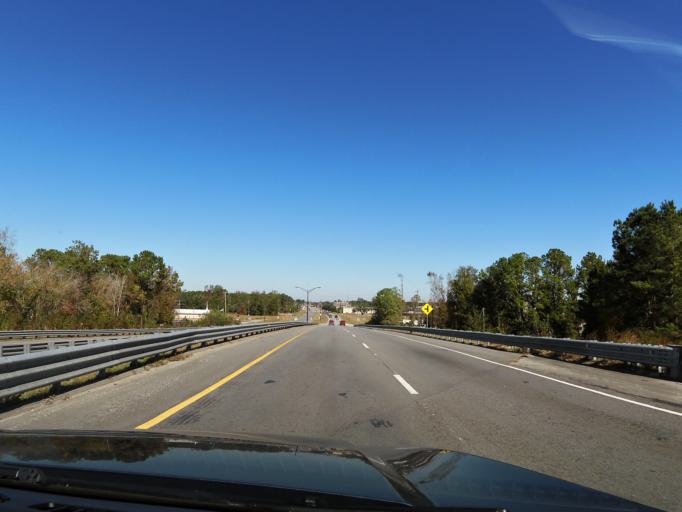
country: US
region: Georgia
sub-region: Bryan County
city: Richmond Hill
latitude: 31.9376
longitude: -81.3195
